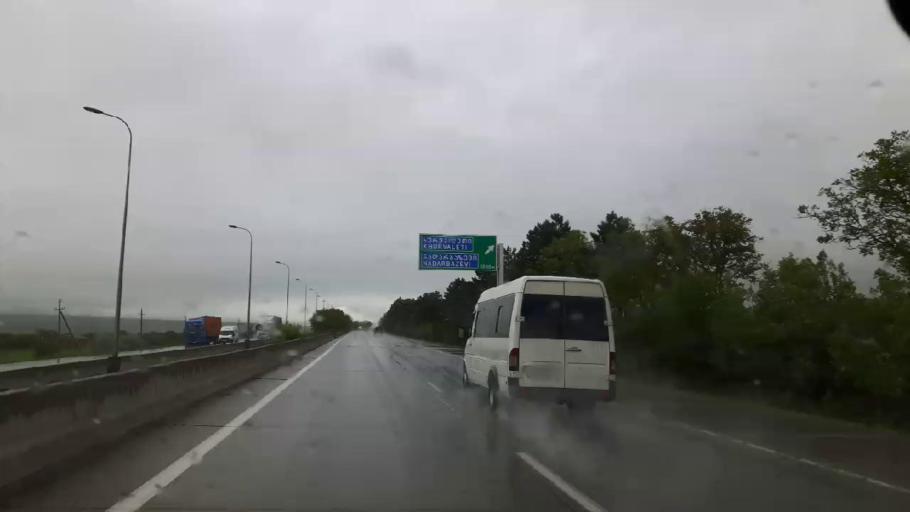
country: GE
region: Shida Kartli
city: Gori
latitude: 42.0229
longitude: 44.2827
